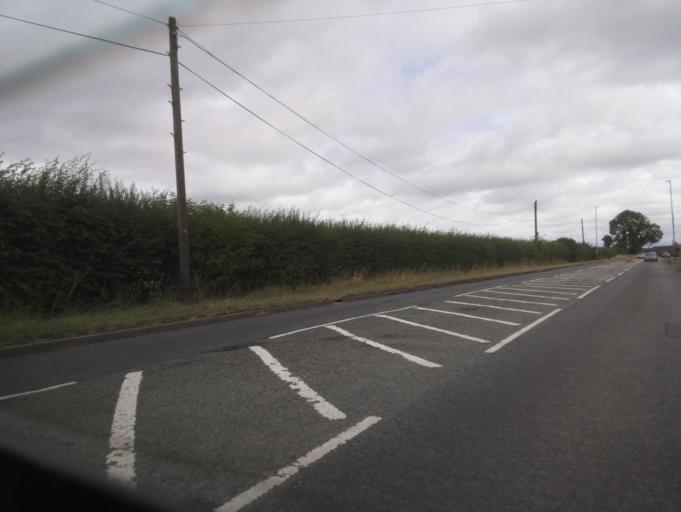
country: GB
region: England
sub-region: Derbyshire
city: Ripley
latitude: 53.0021
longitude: -1.3876
